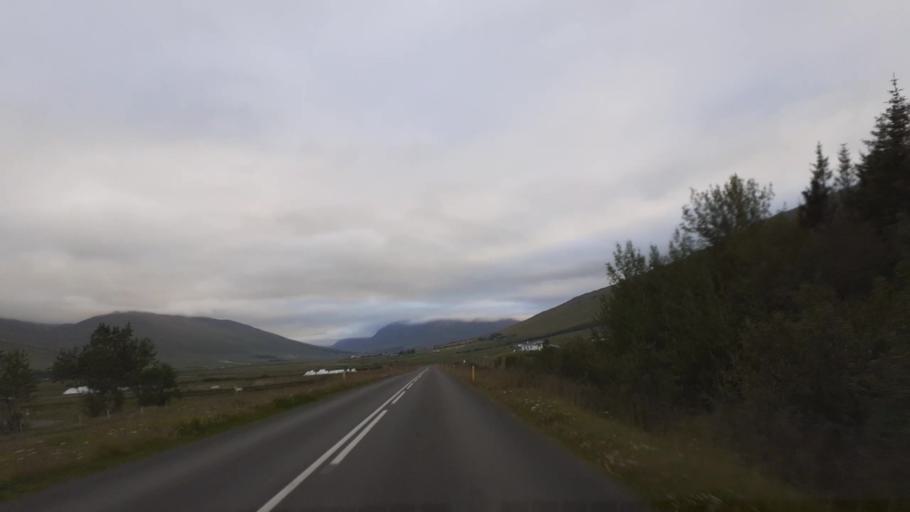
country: IS
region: Northeast
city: Dalvik
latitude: 65.9505
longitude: -18.5546
